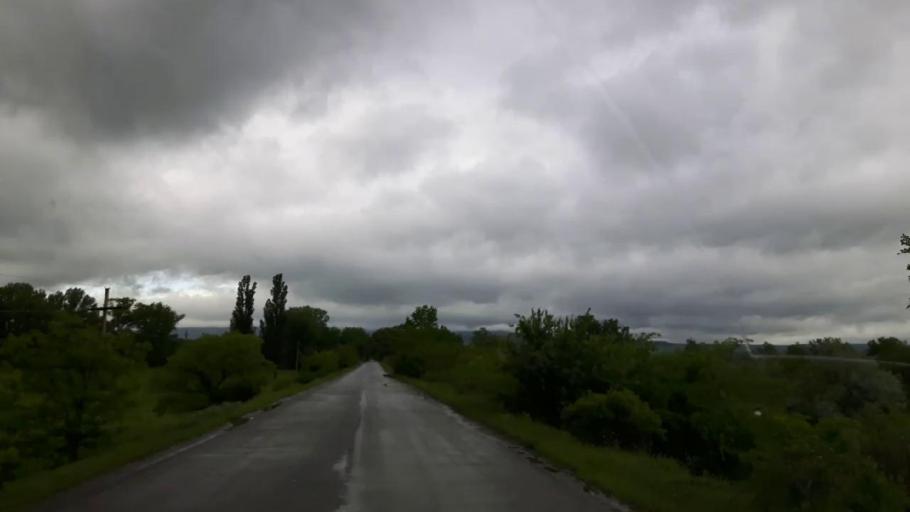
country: GE
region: Shida Kartli
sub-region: Khashuris Raioni
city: Khashuri
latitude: 41.9939
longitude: 43.6573
